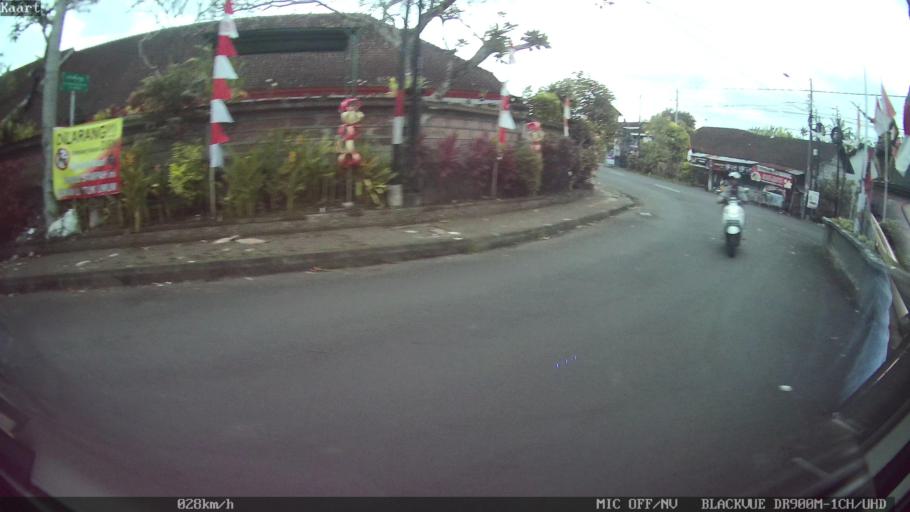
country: ID
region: Bali
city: Banjar Tegal Belodan
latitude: -8.5402
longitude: 115.1190
